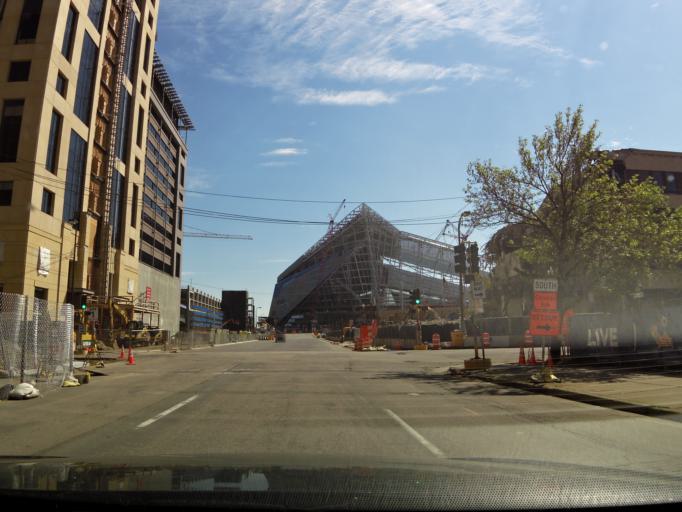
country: US
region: Minnesota
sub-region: Hennepin County
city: Minneapolis
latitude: 44.9765
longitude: -93.2620
